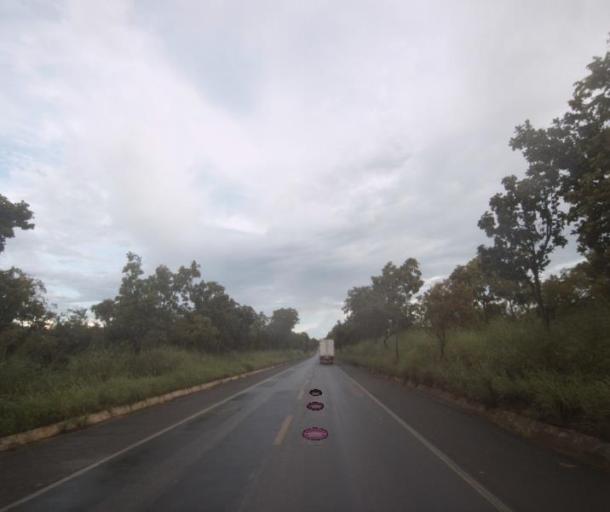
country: BR
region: Goias
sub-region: Porangatu
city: Porangatu
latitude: -13.7847
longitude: -49.0334
